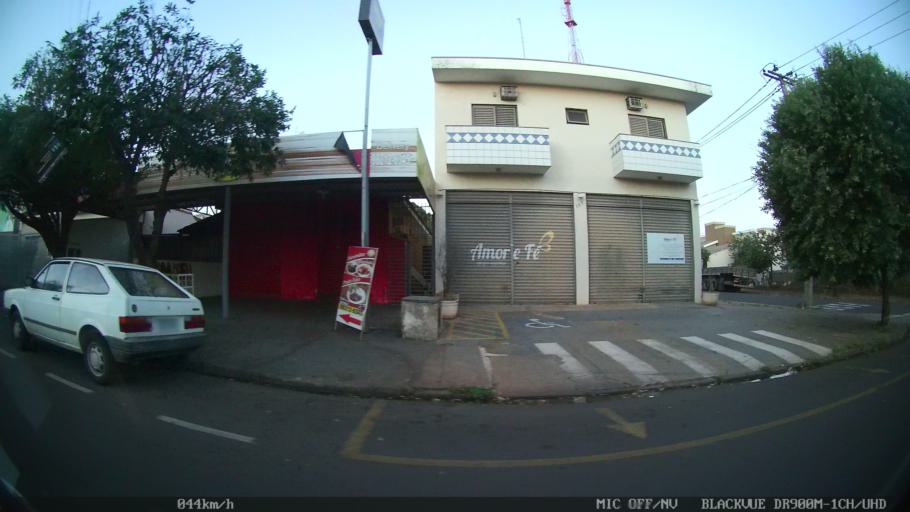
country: BR
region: Sao Paulo
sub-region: Sao Jose Do Rio Preto
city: Sao Jose do Rio Preto
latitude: -20.8035
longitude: -49.3483
